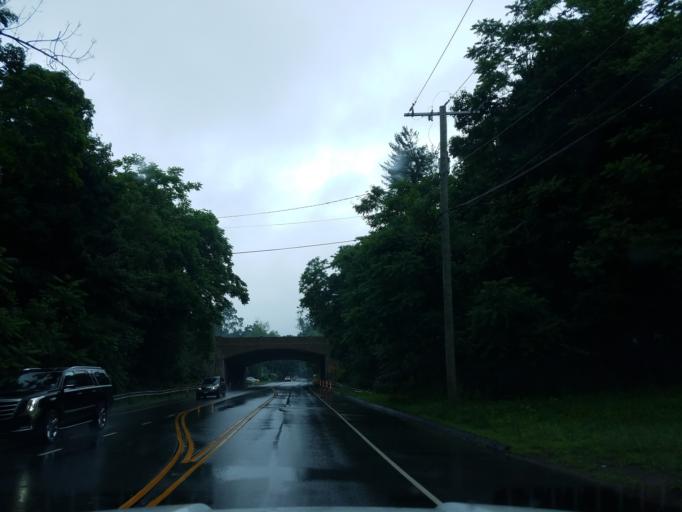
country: US
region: Connecticut
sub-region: Fairfield County
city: Westport
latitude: 41.1633
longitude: -73.3574
